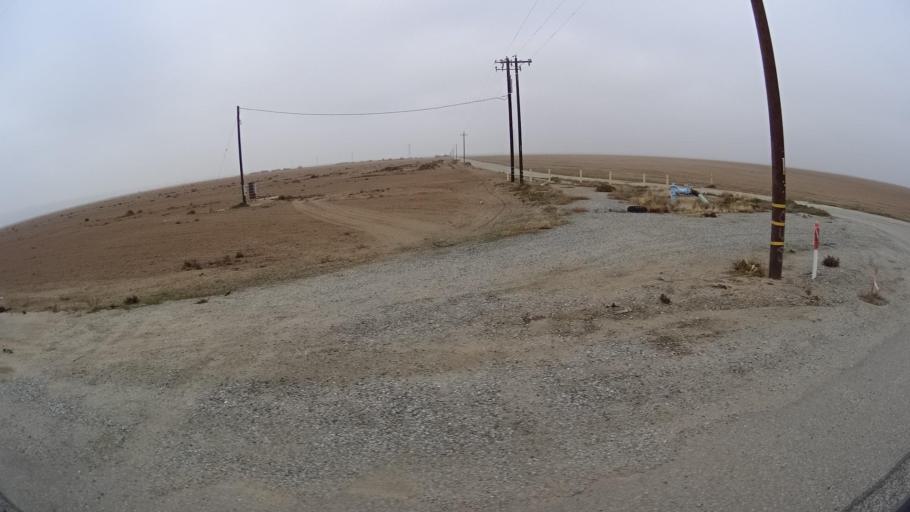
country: US
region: California
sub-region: Kern County
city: Maricopa
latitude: 35.1229
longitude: -119.3052
